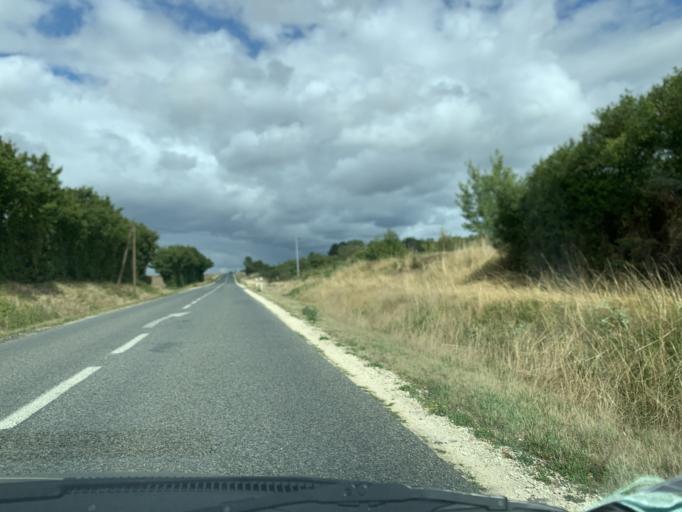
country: FR
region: Bourgogne
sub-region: Departement de la Nievre
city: Clamecy
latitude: 47.4339
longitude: 3.4835
